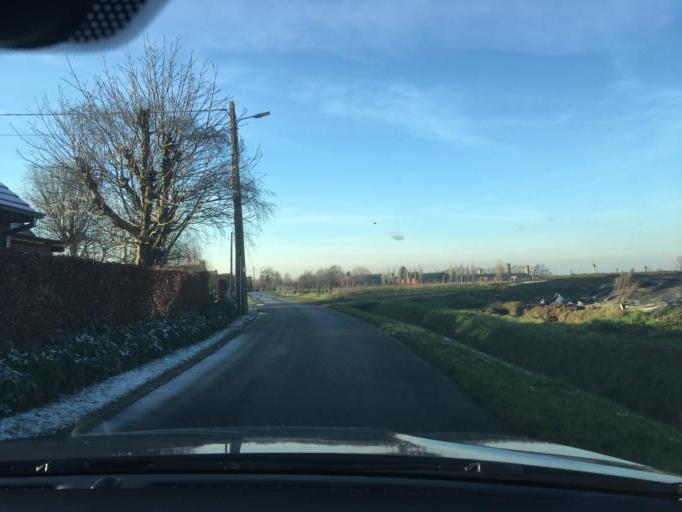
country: BE
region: Flanders
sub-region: Provincie West-Vlaanderen
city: Meulebeke
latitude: 50.9624
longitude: 3.2781
